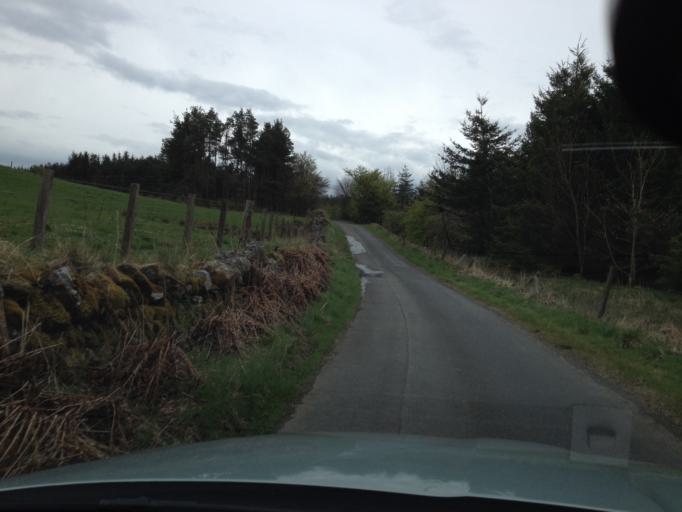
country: GB
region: Scotland
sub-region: West Lothian
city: Linlithgow
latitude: 55.9371
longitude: -3.6058
